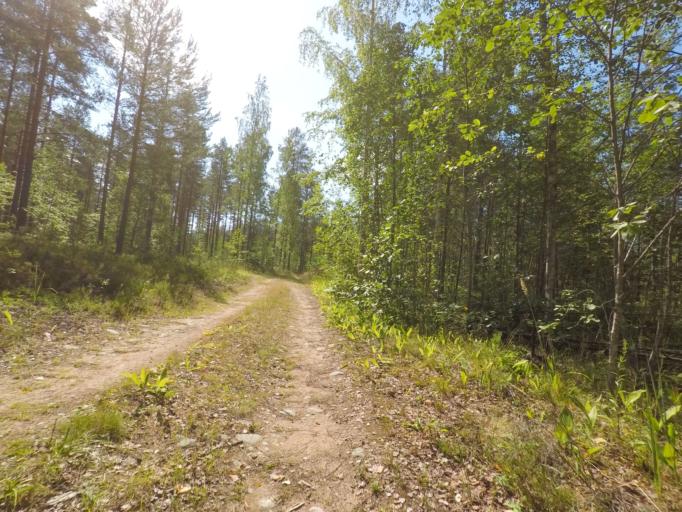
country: FI
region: Southern Savonia
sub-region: Mikkeli
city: Puumala
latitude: 61.5172
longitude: 28.1662
